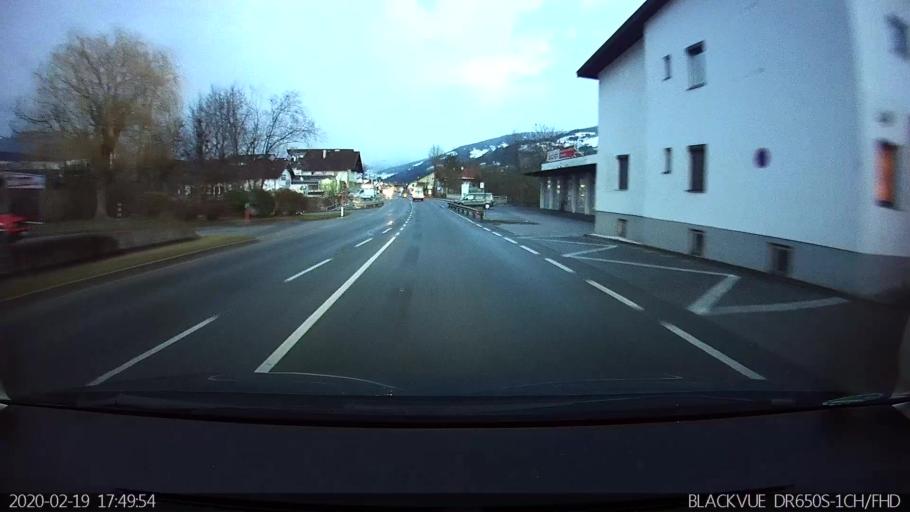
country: AT
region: Tyrol
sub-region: Politischer Bezirk Innsbruck Land
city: Hall in Tirol
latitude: 47.2801
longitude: 11.5261
